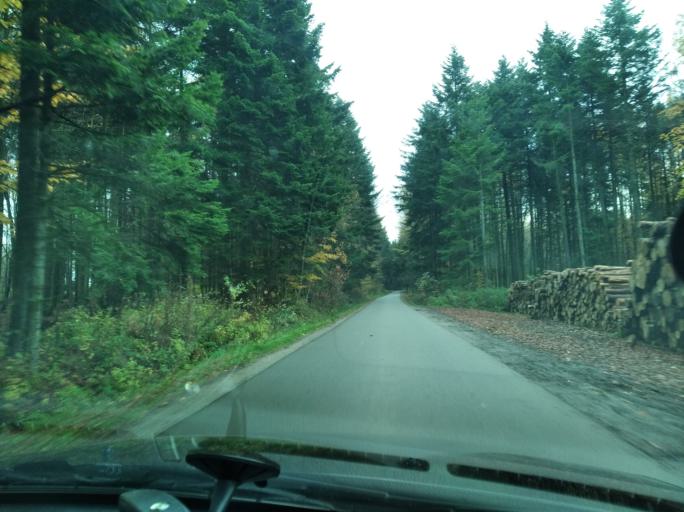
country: PL
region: Subcarpathian Voivodeship
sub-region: Powiat strzyzowski
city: Strzyzow
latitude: 49.9066
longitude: 21.7819
